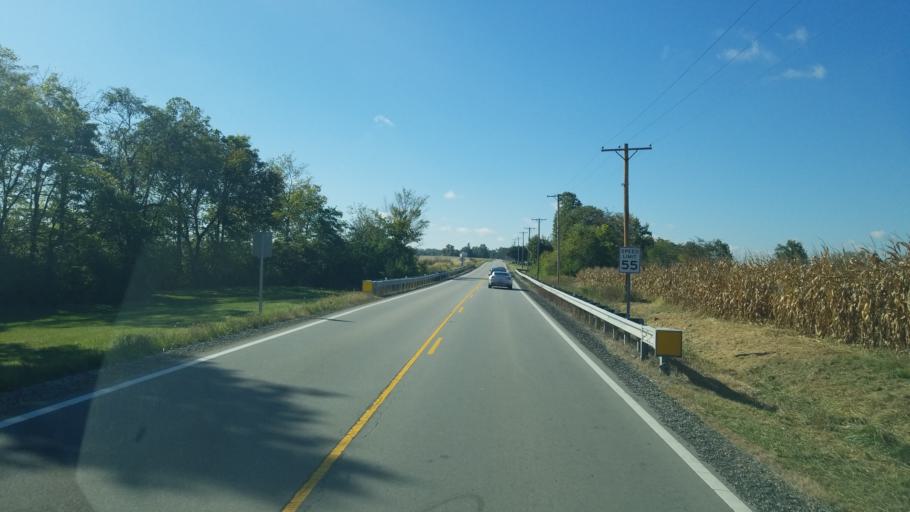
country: US
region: Ohio
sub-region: Fayette County
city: Washington Court House
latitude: 39.4717
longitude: -83.4848
